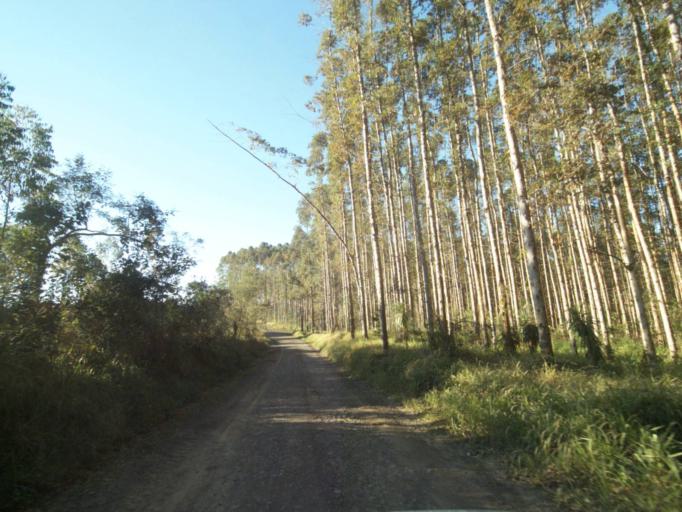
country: BR
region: Parana
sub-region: Telemaco Borba
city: Telemaco Borba
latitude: -24.4908
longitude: -50.5946
